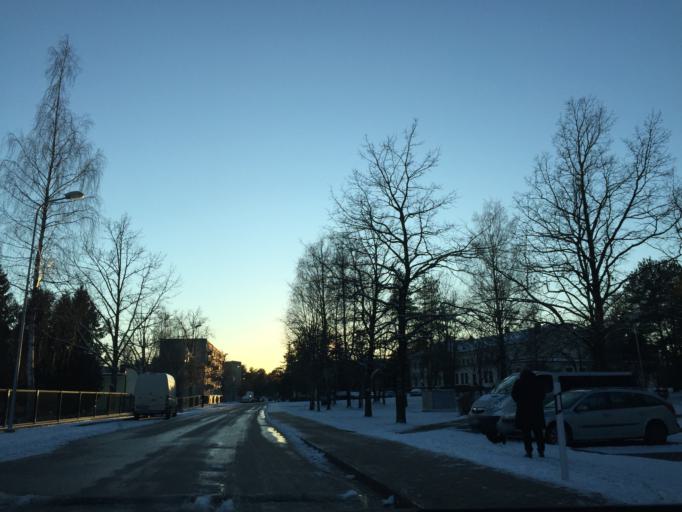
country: LV
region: Kekava
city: Balozi
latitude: 56.8779
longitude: 24.1201
